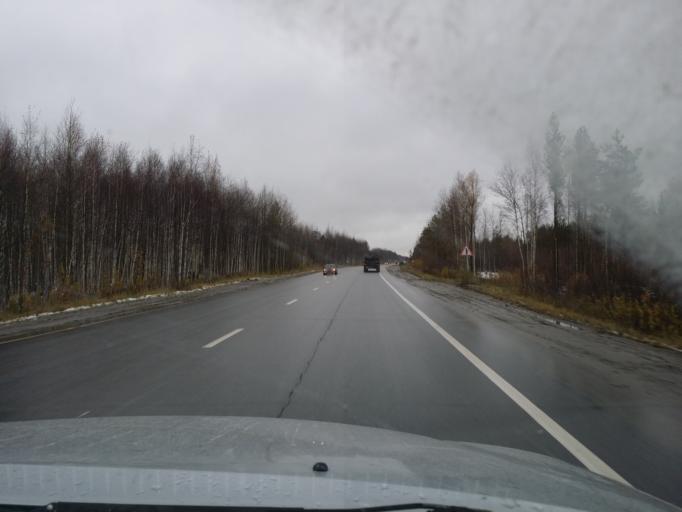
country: RU
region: Khanty-Mansiyskiy Avtonomnyy Okrug
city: Megion
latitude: 61.0931
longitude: 76.0817
